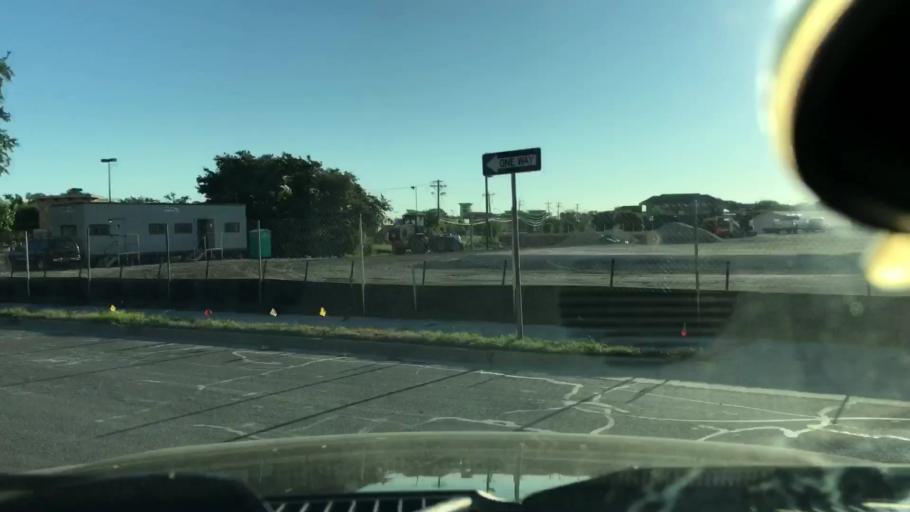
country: US
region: Texas
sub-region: Williamson County
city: Cedar Park
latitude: 30.5217
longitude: -97.8230
